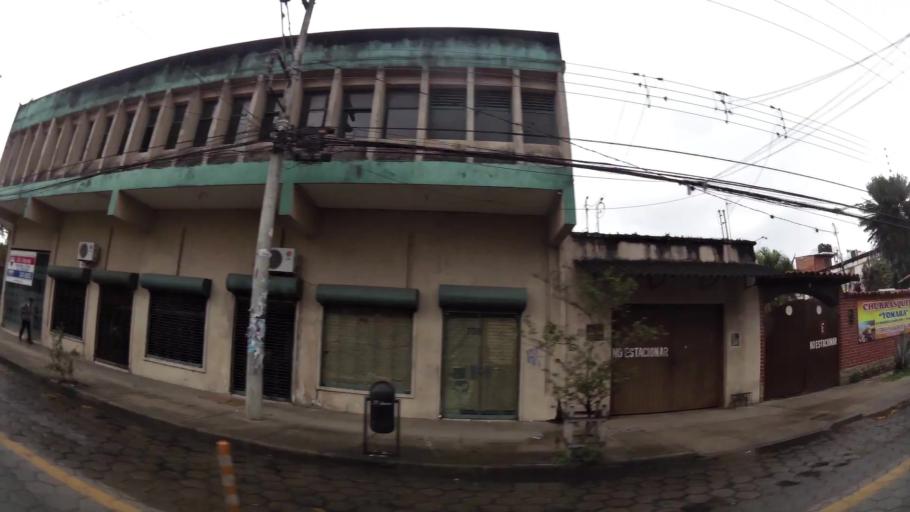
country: BO
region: Santa Cruz
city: Santa Cruz de la Sierra
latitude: -17.7831
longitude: -63.1737
